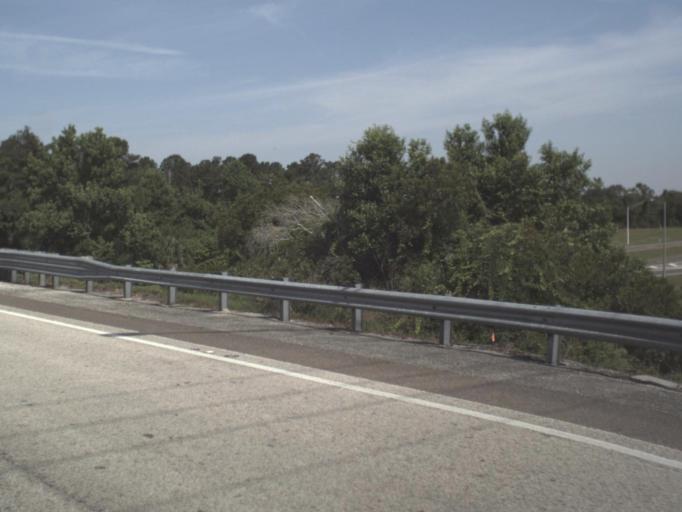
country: US
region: Florida
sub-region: Duval County
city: Jacksonville
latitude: 30.2501
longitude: -81.5518
